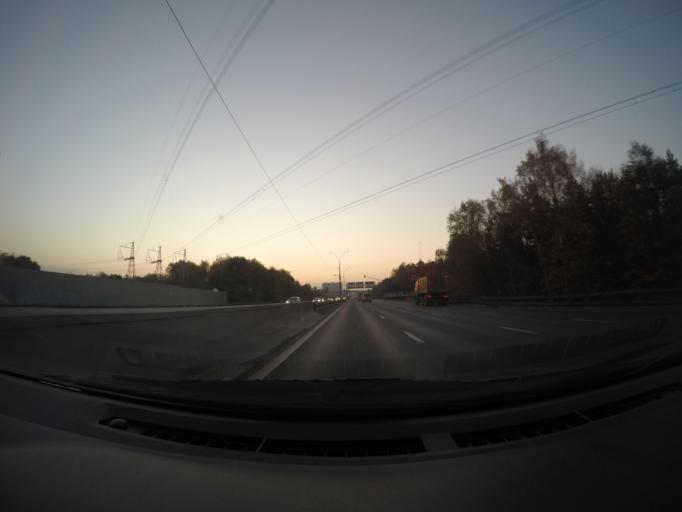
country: RU
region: Moscow
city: Vykhino-Zhulebino
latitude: 55.6914
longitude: 37.8197
